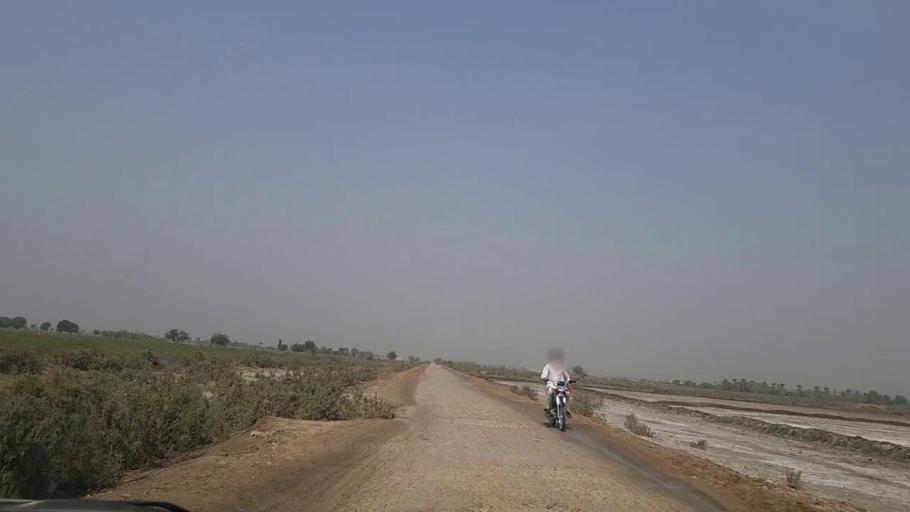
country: PK
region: Sindh
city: Pithoro
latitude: 25.5488
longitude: 69.2272
